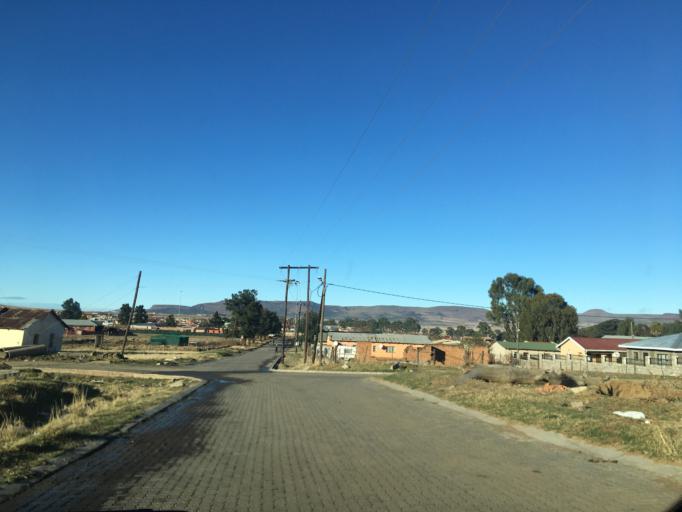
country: ZA
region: Eastern Cape
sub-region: Chris Hani District Municipality
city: Cala
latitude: -31.5278
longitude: 27.6959
